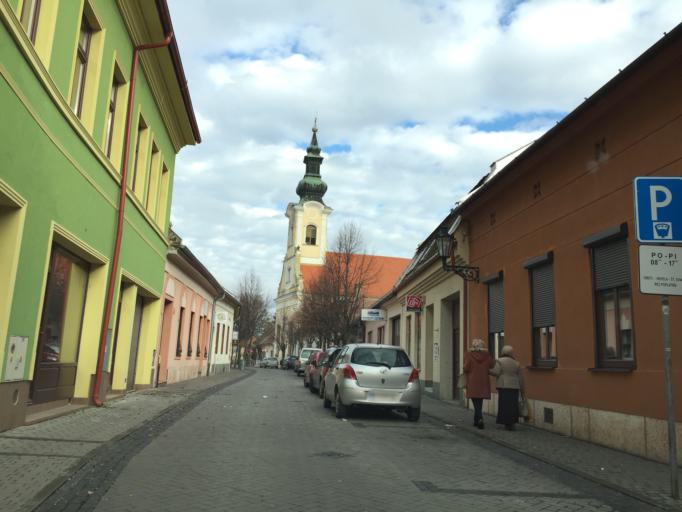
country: SK
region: Nitriansky
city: Komarno
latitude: 47.7582
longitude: 18.1306
